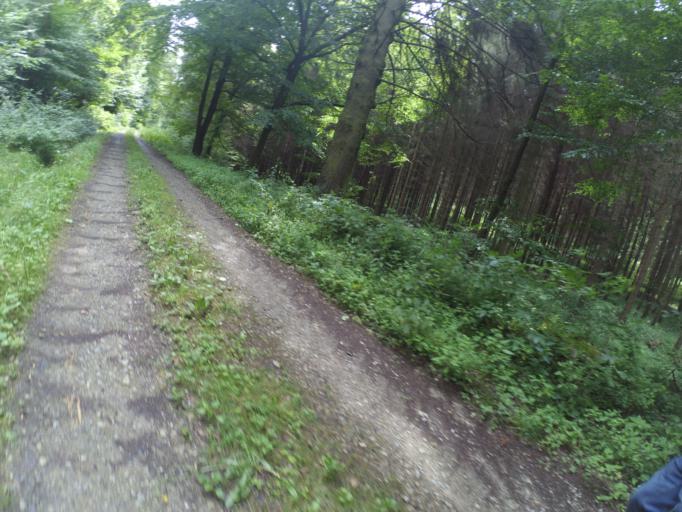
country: DE
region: Hesse
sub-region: Regierungsbezirk Kassel
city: Kirchheim
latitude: 50.8663
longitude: 9.5378
